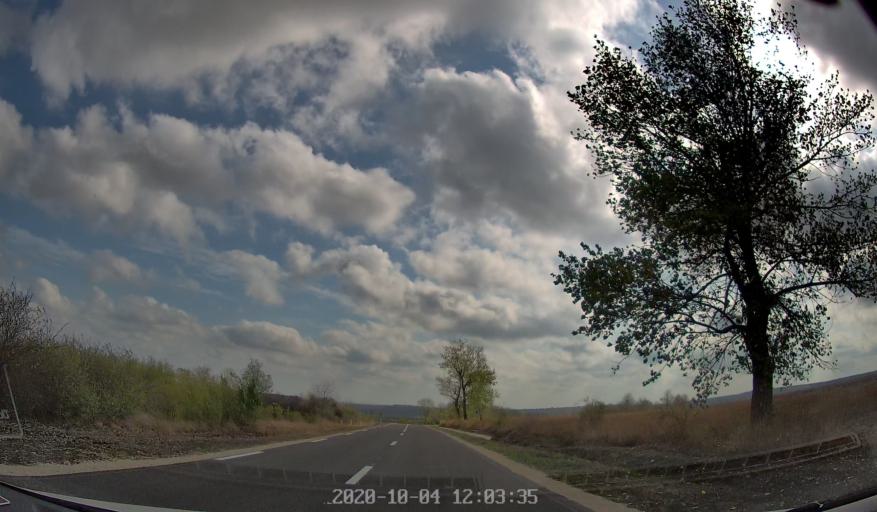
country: MD
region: Rezina
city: Saharna
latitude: 47.6109
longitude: 28.9297
